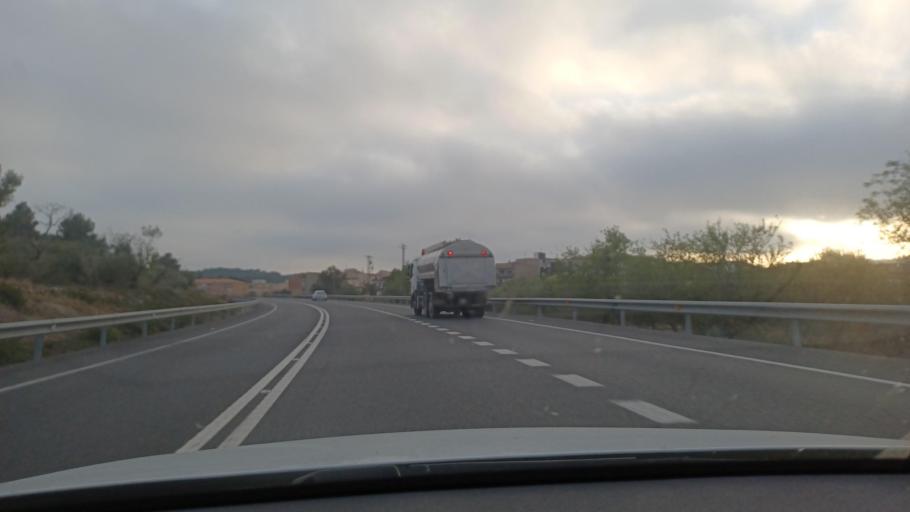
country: ES
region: Catalonia
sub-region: Provincia de Tarragona
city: El Perello
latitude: 40.8757
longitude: 0.7156
